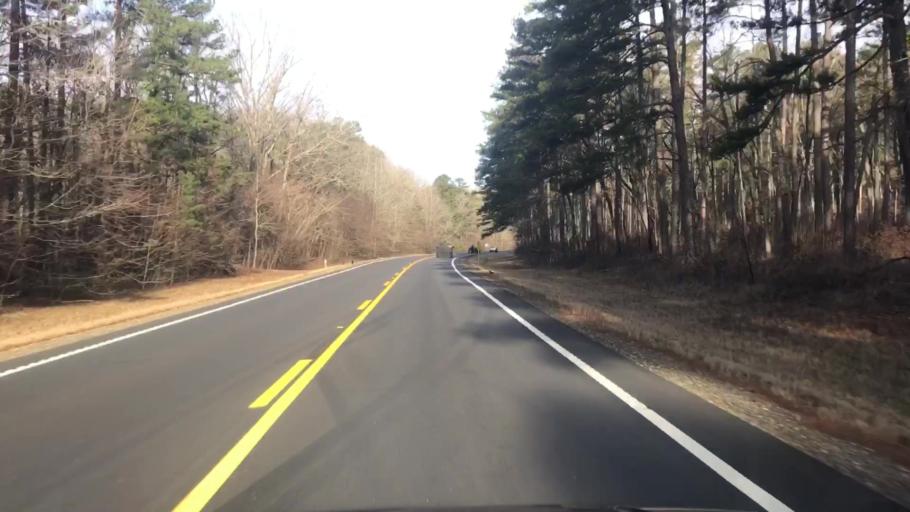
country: US
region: Arkansas
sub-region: Montgomery County
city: Mount Ida
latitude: 34.5186
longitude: -93.3874
